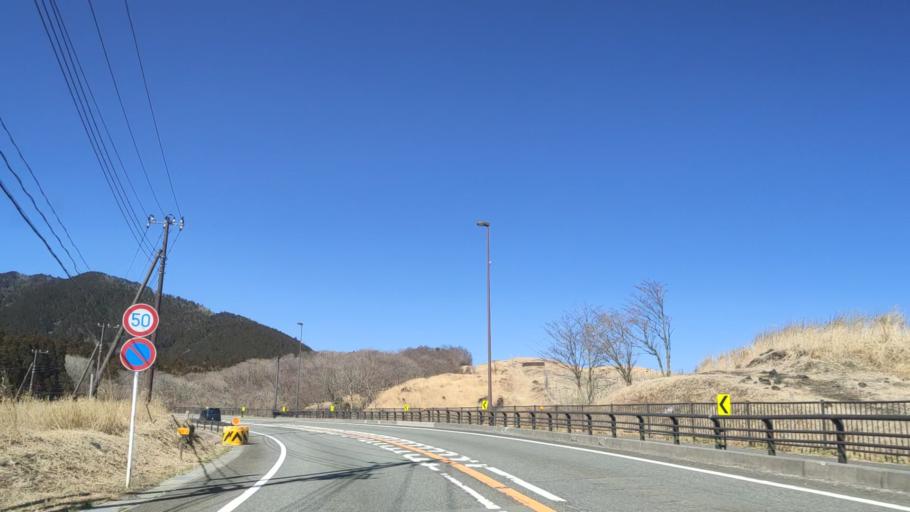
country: JP
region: Yamanashi
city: Fujikawaguchiko
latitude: 35.4239
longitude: 138.5926
